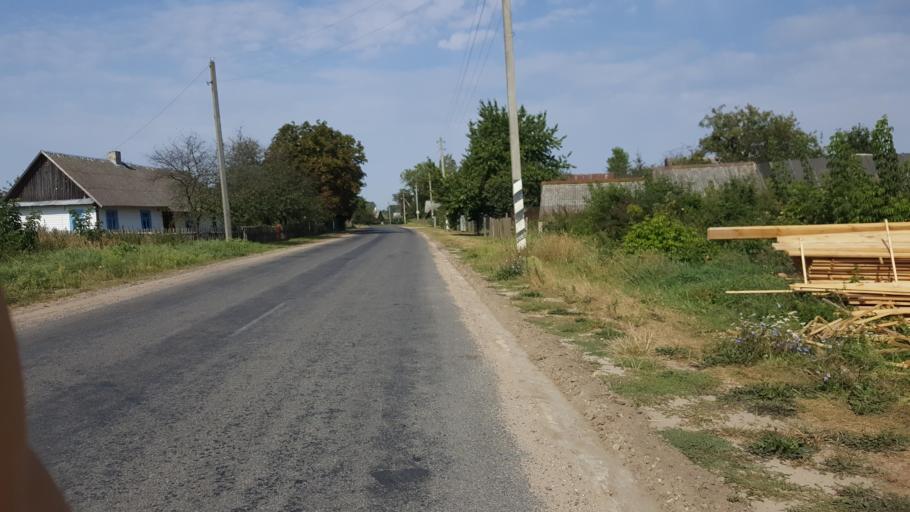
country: BY
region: Brest
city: Kamyanyets
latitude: 52.4287
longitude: 23.7580
